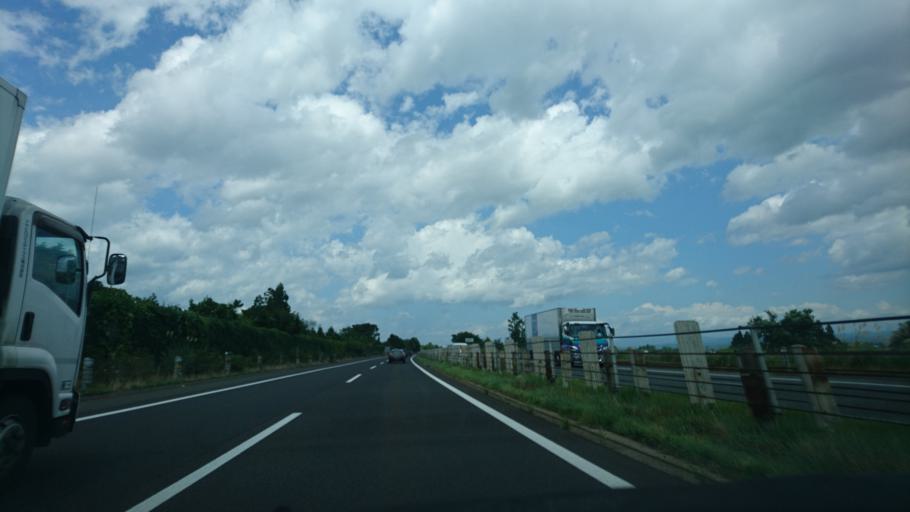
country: JP
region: Iwate
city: Morioka-shi
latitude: 39.5888
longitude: 141.1175
